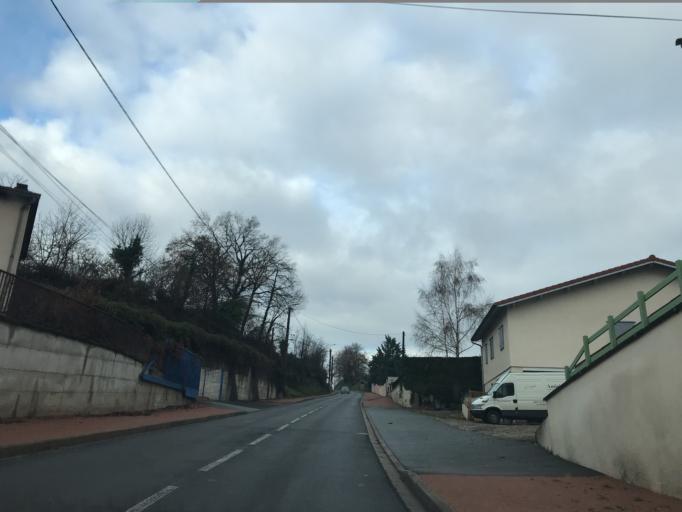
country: FR
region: Auvergne
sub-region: Departement du Puy-de-Dome
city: Thiers
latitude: 45.8524
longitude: 3.5332
